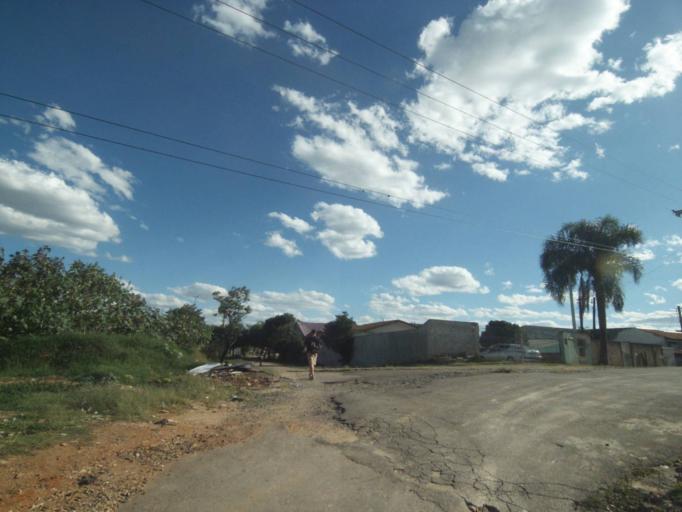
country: BR
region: Parana
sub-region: Curitiba
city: Curitiba
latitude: -25.4973
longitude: -49.3365
